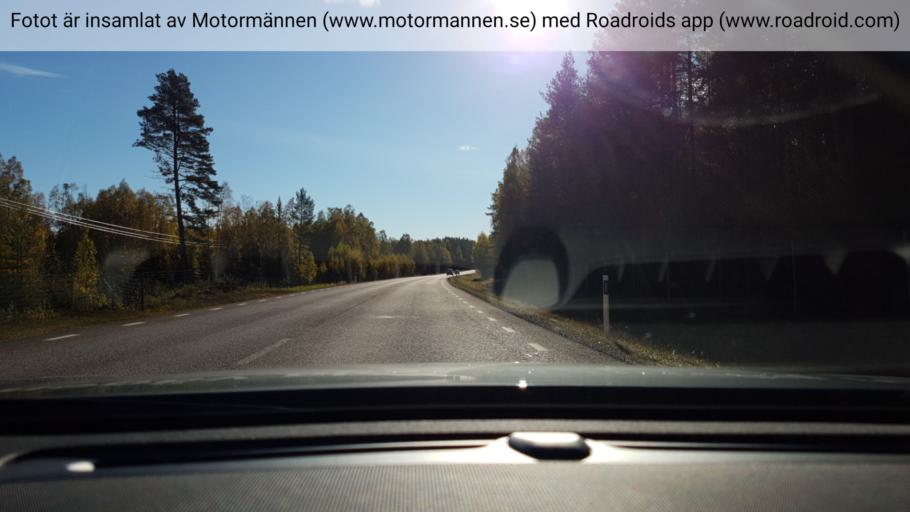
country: SE
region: Vaesterbotten
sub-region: Skelleftea Kommun
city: Burea
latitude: 64.6048
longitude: 21.1986
